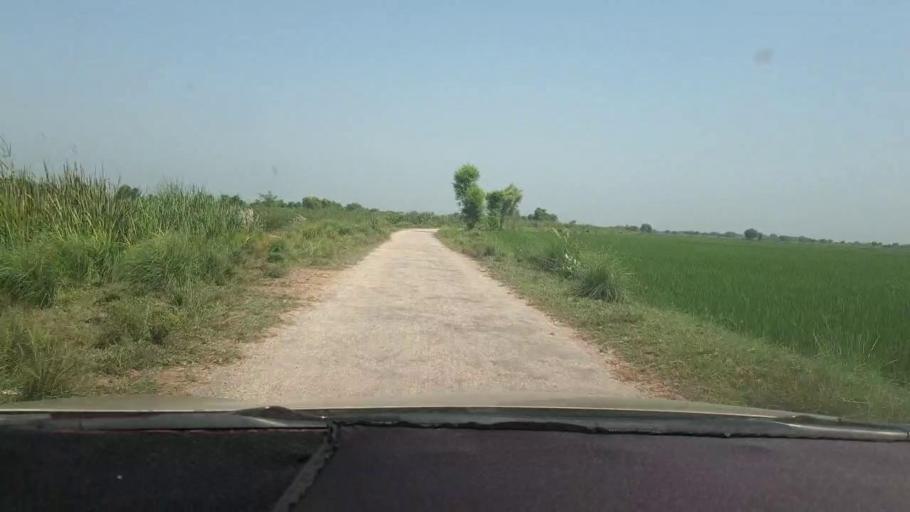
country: PK
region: Sindh
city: Miro Khan
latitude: 27.7017
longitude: 68.0896
